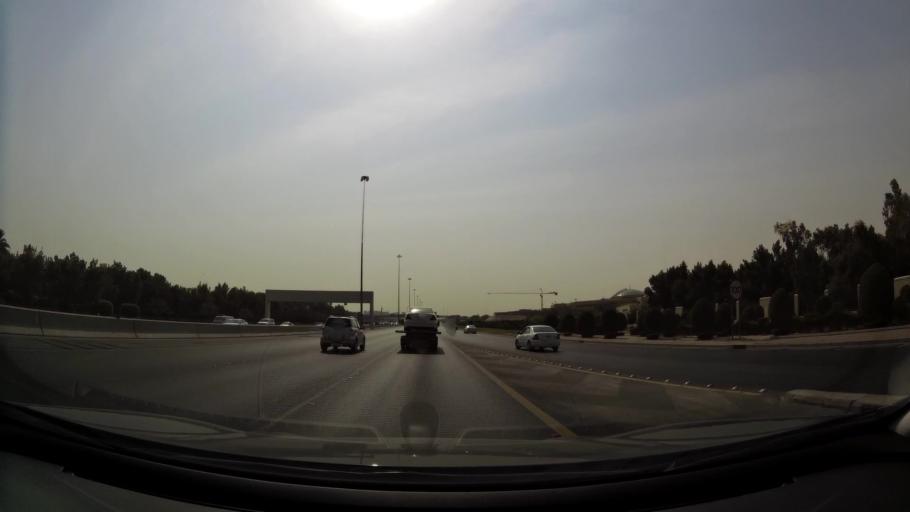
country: KW
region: Al Asimah
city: Ar Rabiyah
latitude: 29.2982
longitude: 47.9460
